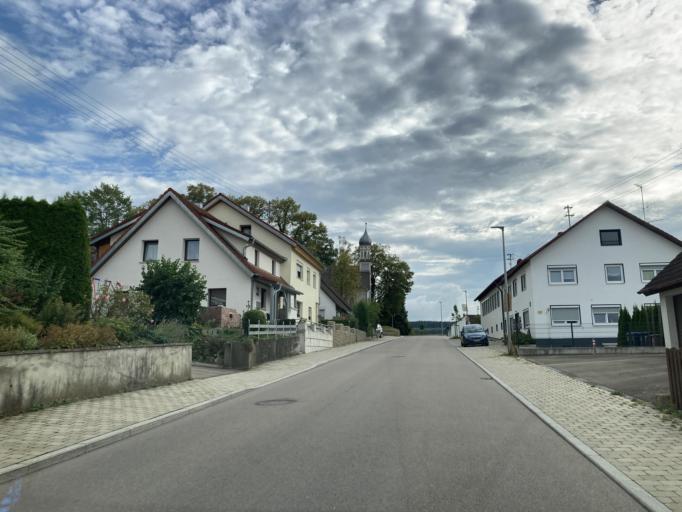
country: DE
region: Baden-Wuerttemberg
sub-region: Regierungsbezirk Stuttgart
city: Dischingen
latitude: 48.6921
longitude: 10.3643
